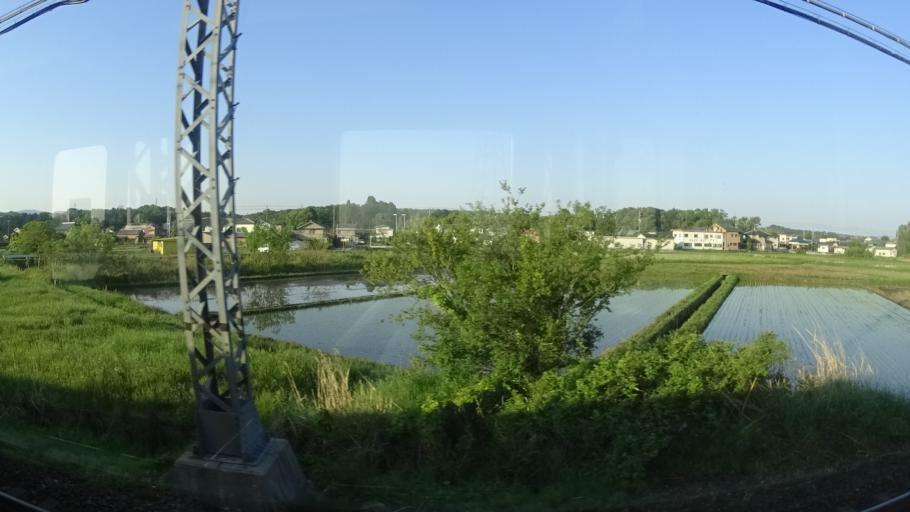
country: JP
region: Mie
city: Ise
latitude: 34.5269
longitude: 136.6544
